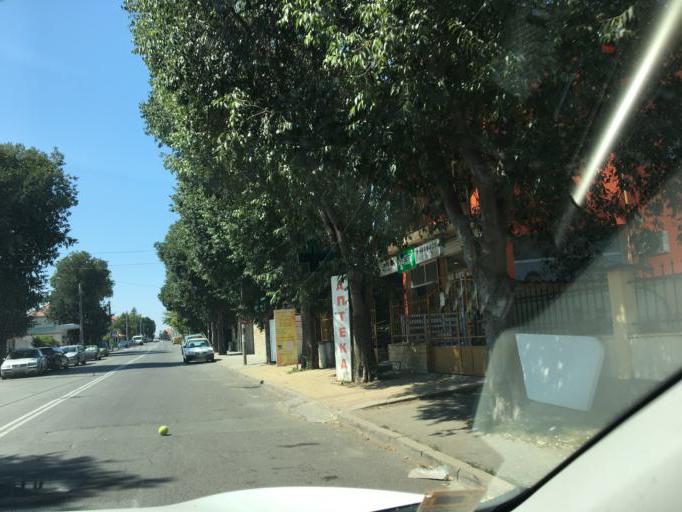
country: BG
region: Burgas
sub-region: Obshtina Kameno
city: Kameno
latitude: 42.6066
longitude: 27.3874
